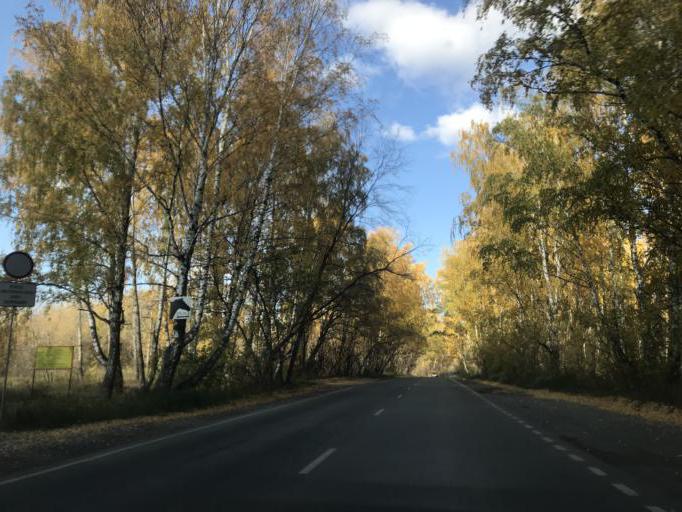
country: RU
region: Chelyabinsk
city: Dolgoderevenskoye
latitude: 55.2602
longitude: 61.3637
